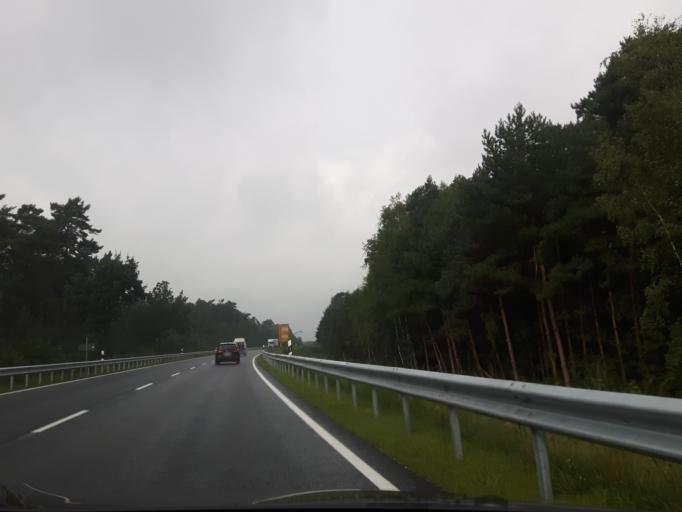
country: DE
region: Lower Saxony
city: Lingen
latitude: 52.4916
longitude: 7.3111
